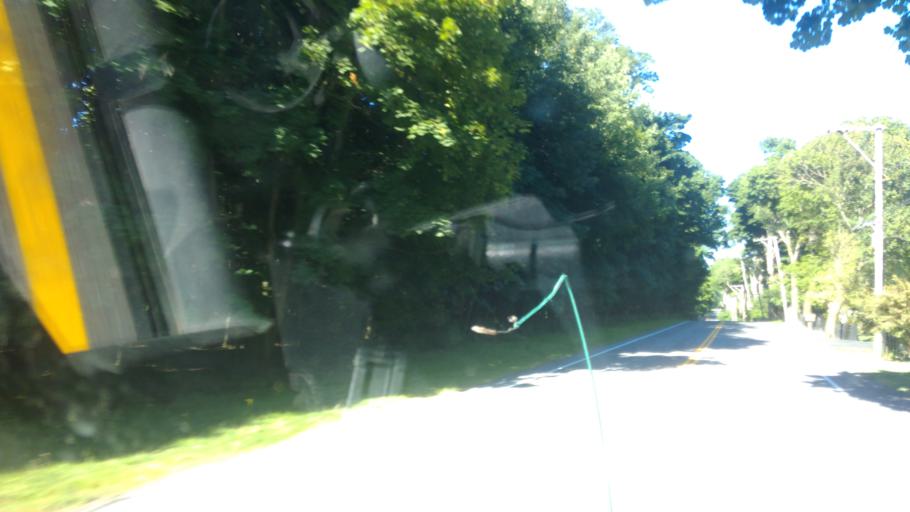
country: US
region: New York
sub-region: Monroe County
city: Webster
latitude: 43.2580
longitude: -77.4606
